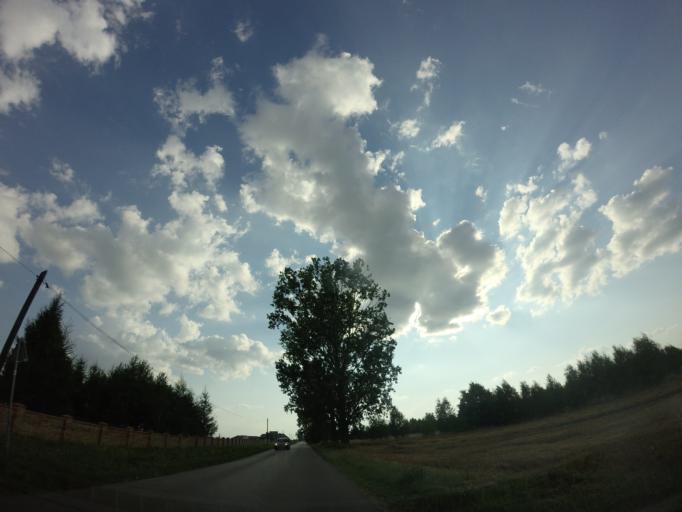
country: PL
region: Lublin Voivodeship
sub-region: Powiat lukowski
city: Wojcieszkow
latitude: 51.7666
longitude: 22.3057
